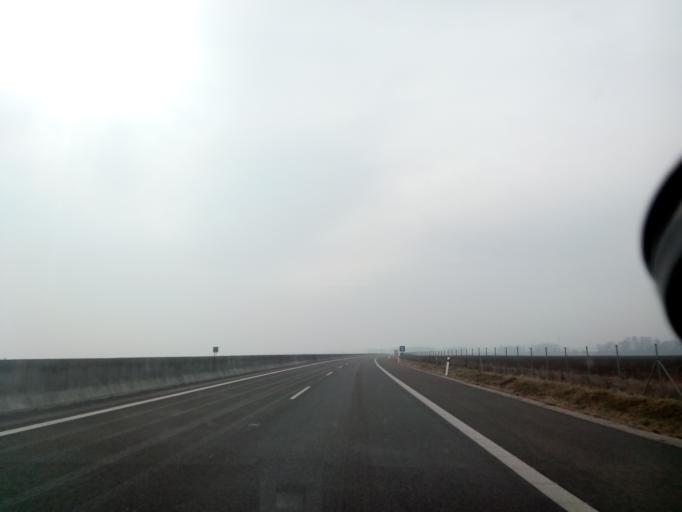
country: HU
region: Borsod-Abauj-Zemplen
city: Gonc
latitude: 48.5855
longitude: 21.2478
